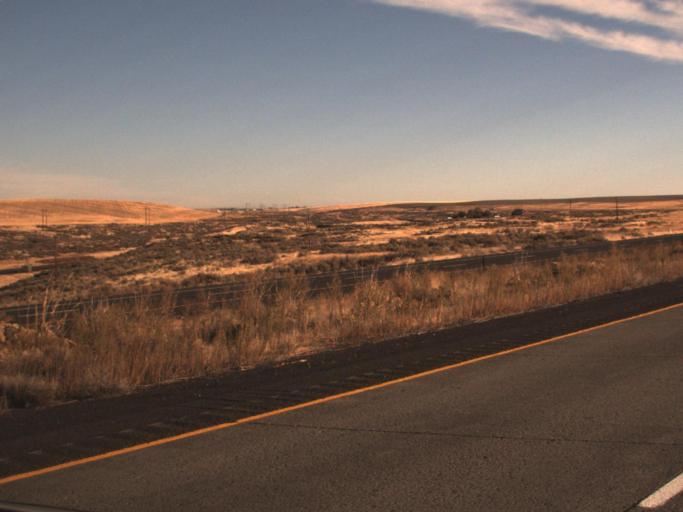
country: US
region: Washington
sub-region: Adams County
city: Ritzville
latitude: 47.0545
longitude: -118.4203
